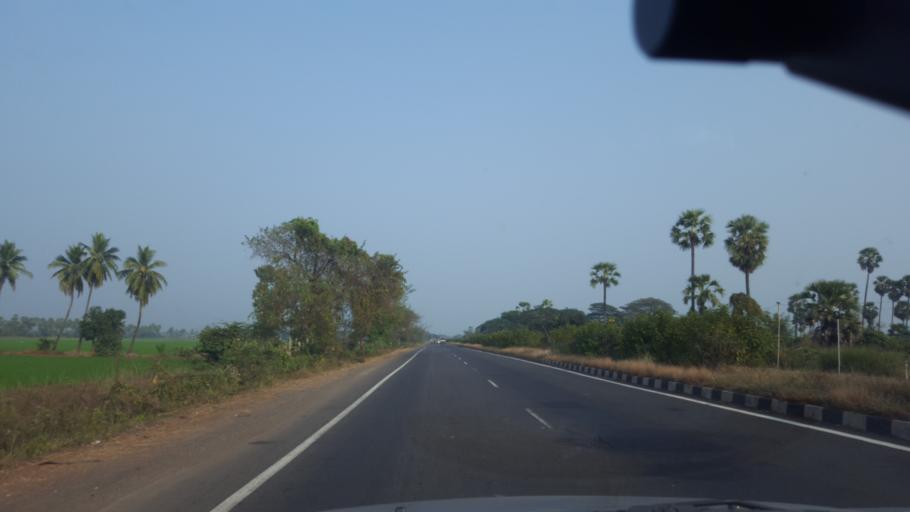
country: IN
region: Andhra Pradesh
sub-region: West Godavari
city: Tadepallegudem
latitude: 16.8102
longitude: 81.3408
